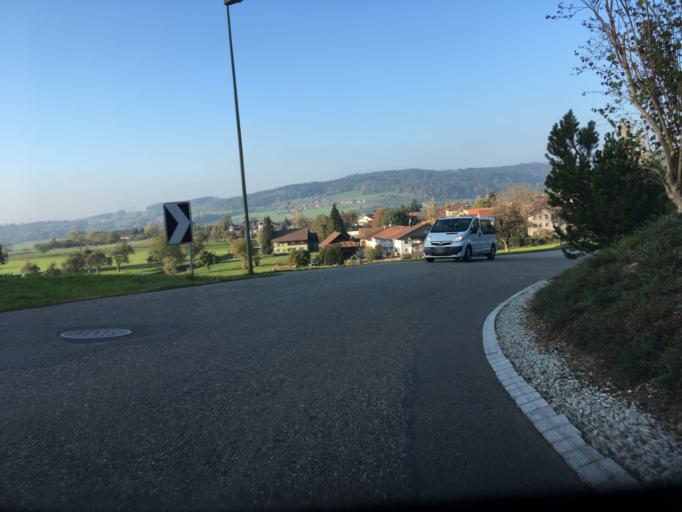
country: CH
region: Zurich
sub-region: Bezirk Pfaeffikon
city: Hittnau / Hittnau (Dorf)
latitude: 47.3568
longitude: 8.8231
